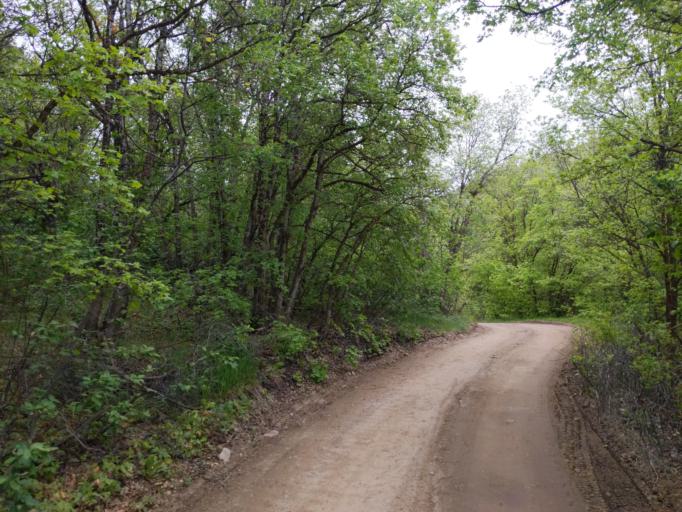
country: US
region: Idaho
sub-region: Bannock County
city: Pocatello
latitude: 42.8242
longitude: -112.4864
